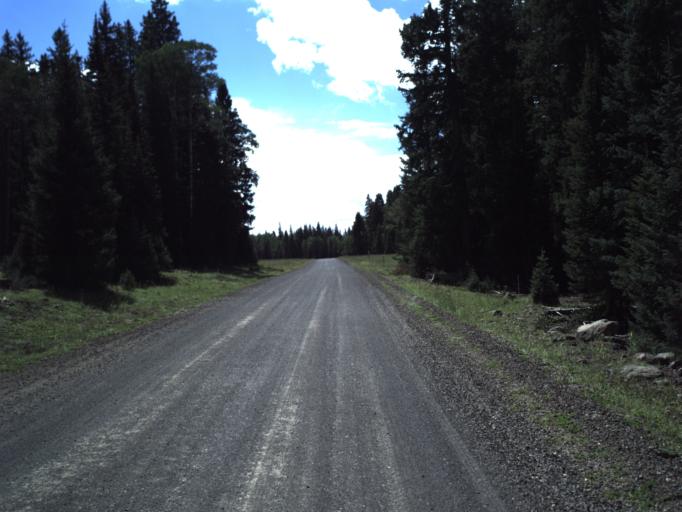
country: US
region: Utah
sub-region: Piute County
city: Junction
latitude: 38.2532
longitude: -112.3765
